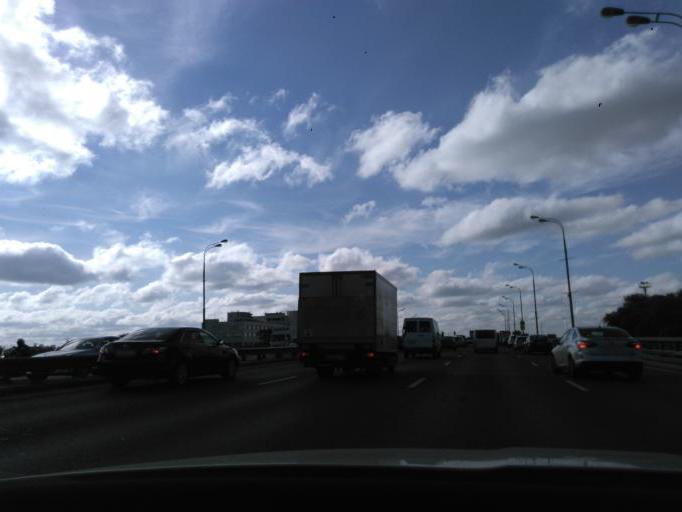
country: RU
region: Moscow
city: Lefortovo
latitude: 55.7280
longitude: 37.7085
